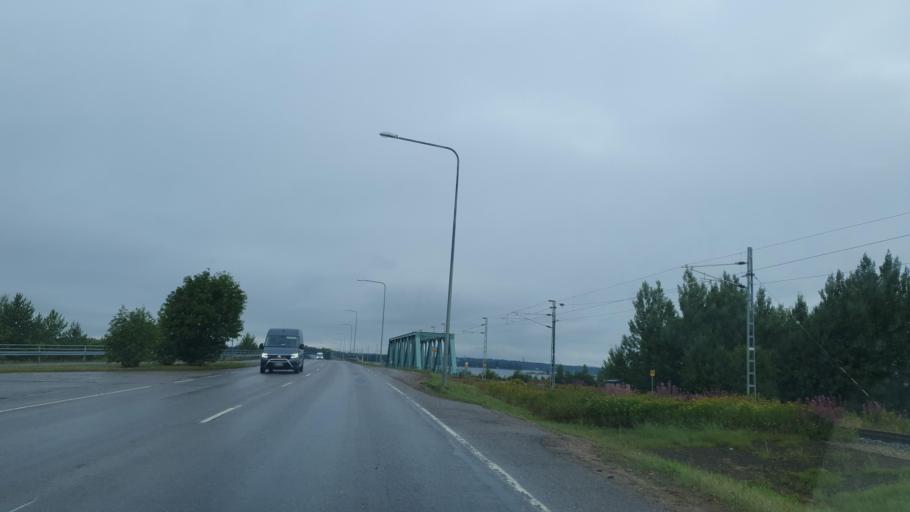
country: FI
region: Lapland
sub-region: Itae-Lappi
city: Kemijaervi
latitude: 66.7157
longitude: 27.4748
